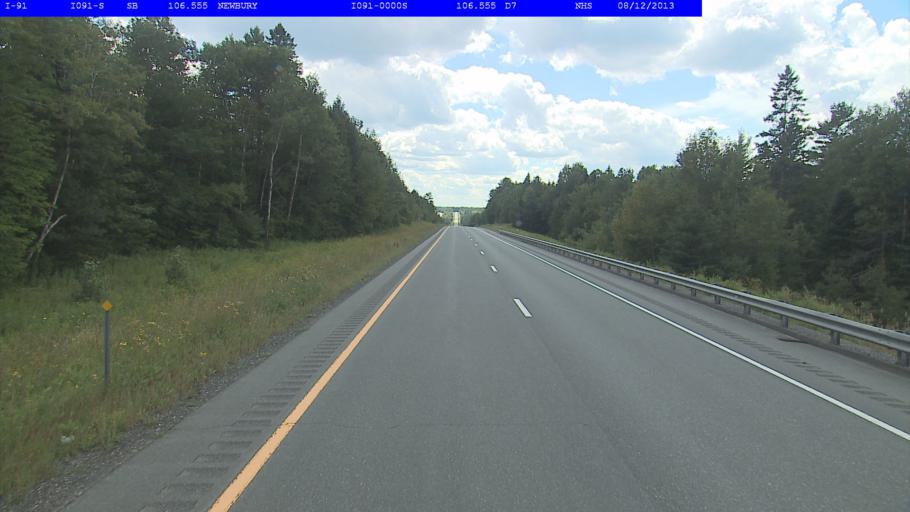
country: US
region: New Hampshire
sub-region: Grafton County
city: Woodsville
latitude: 44.1082
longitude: -72.1083
